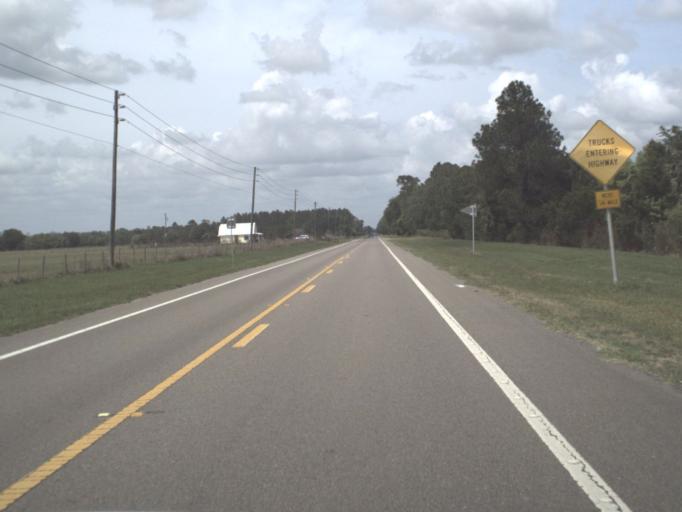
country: US
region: Florida
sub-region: Flagler County
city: Bunnell
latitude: 29.3225
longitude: -81.3103
